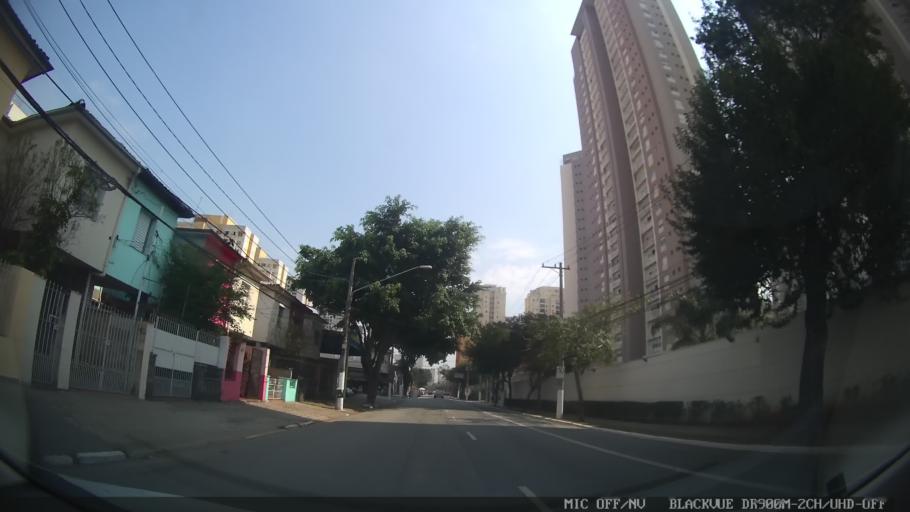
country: BR
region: Sao Paulo
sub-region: Sao Paulo
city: Sao Paulo
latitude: -23.5767
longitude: -46.6034
